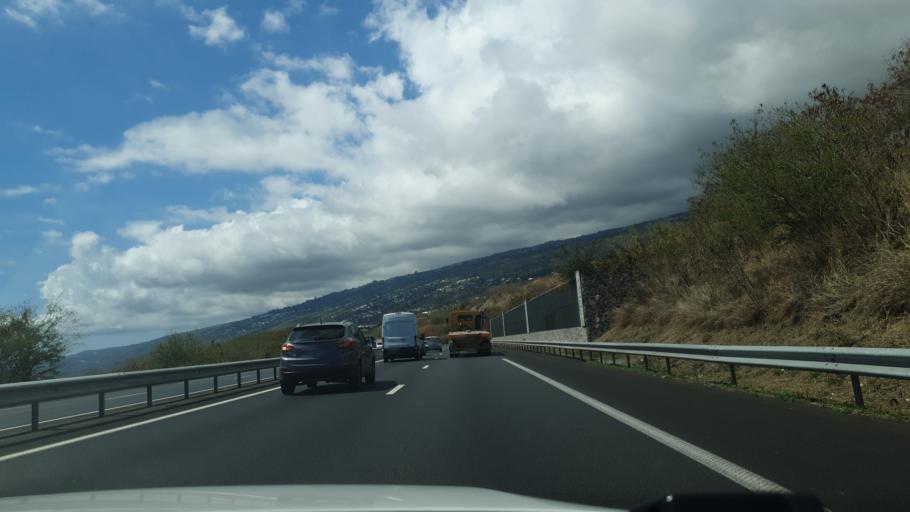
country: RE
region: Reunion
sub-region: Reunion
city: Saint-Leu
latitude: -21.1905
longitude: 55.2965
